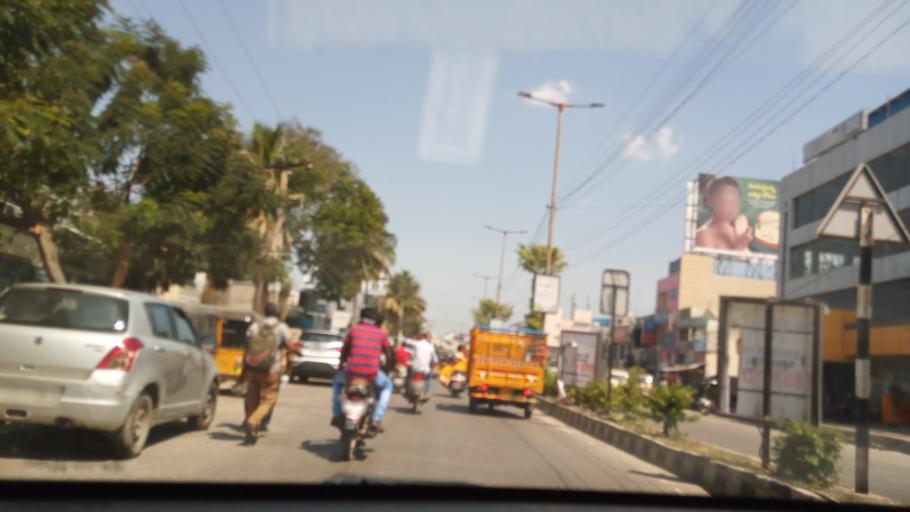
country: IN
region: Andhra Pradesh
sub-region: Chittoor
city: Tirupati
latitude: 13.6228
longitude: 79.4223
